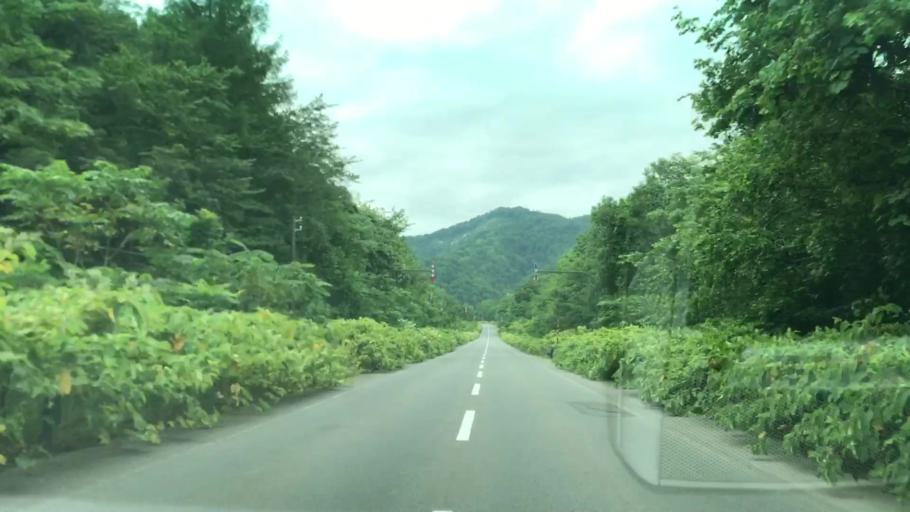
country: JP
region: Hokkaido
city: Yoichi
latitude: 43.0197
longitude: 140.8678
